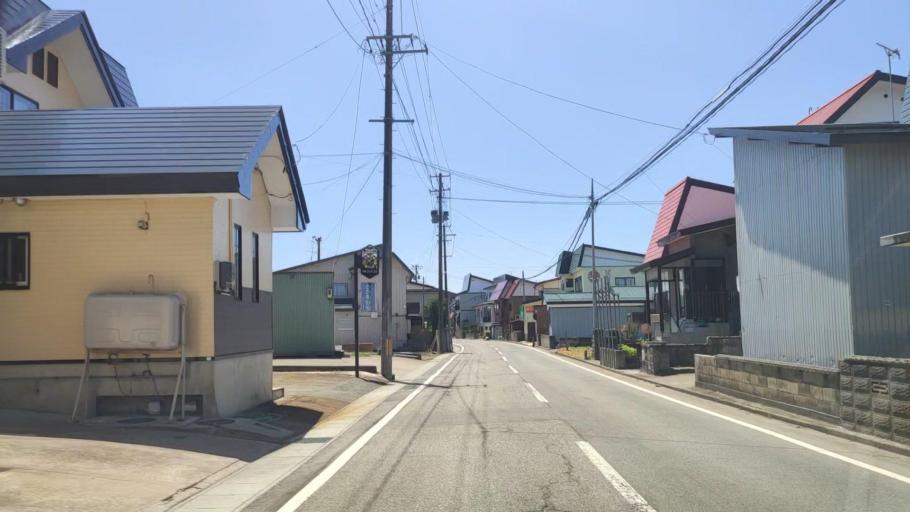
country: JP
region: Yamagata
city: Shinjo
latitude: 38.7740
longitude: 140.3086
